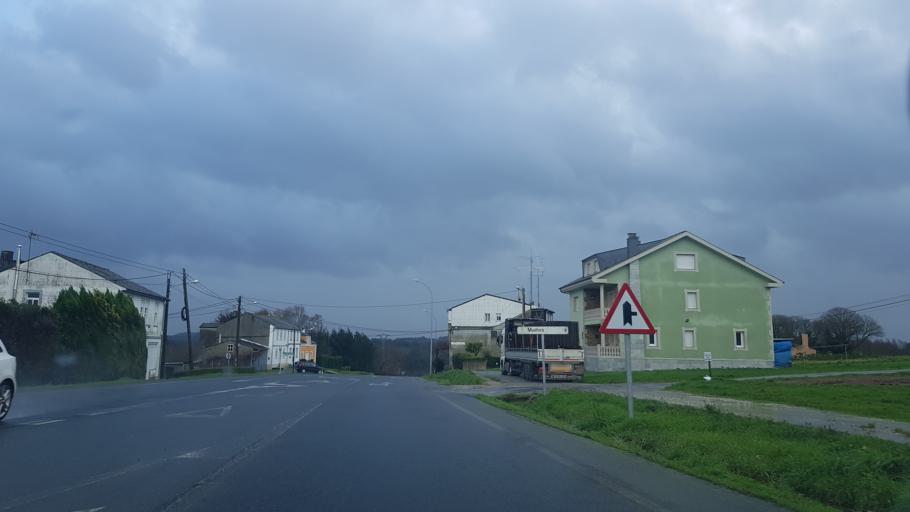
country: ES
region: Galicia
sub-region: Provincia de Lugo
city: Vilalba
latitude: 43.2818
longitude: -7.6763
